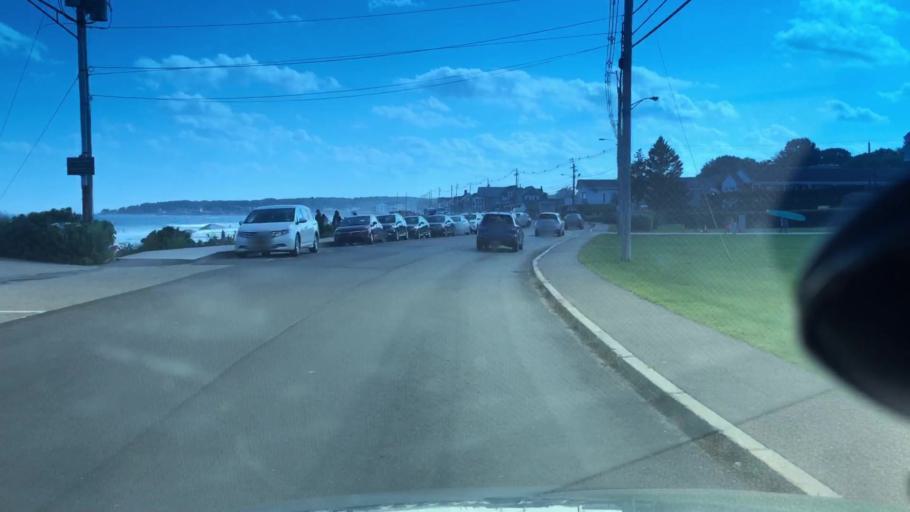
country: US
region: Maine
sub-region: York County
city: York Beach
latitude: 43.1634
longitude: -70.6193
